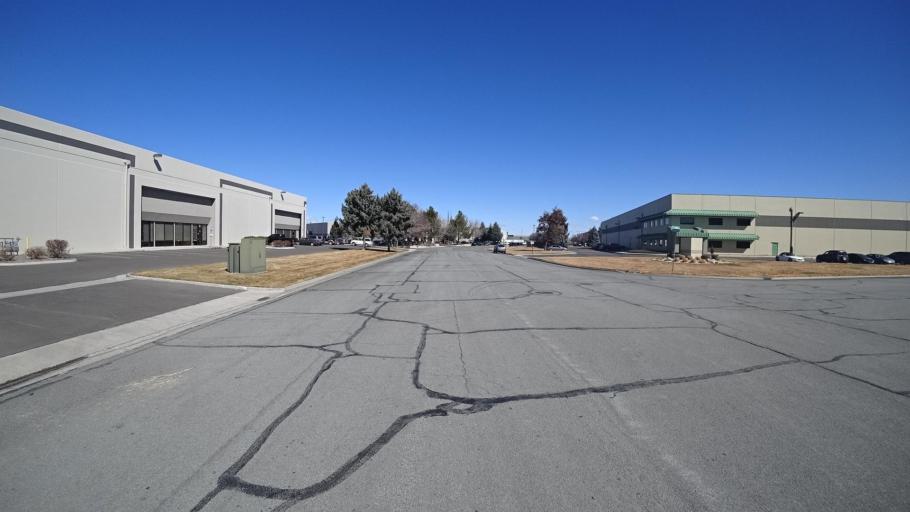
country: US
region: Nevada
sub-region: Washoe County
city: Sparks
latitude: 39.4895
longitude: -119.7627
